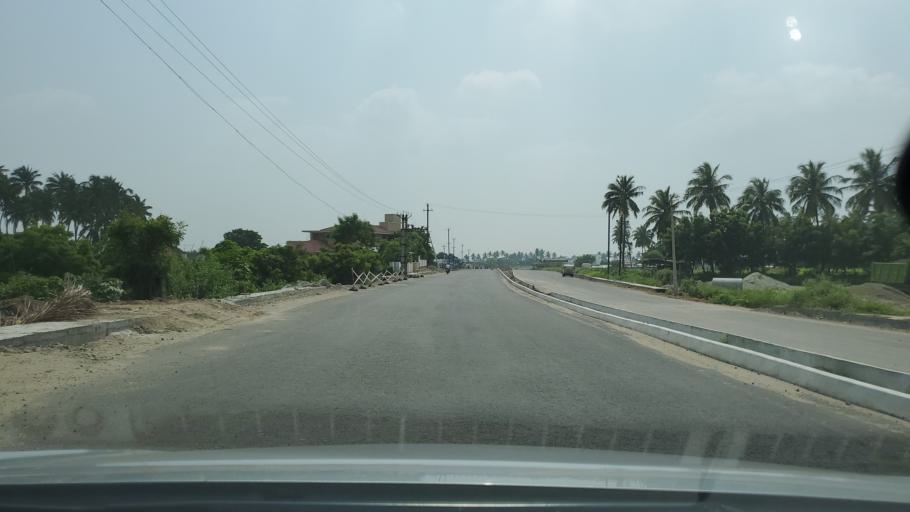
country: IN
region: Tamil Nadu
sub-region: Tiruppur
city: Kangayam
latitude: 10.9383
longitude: 77.4404
